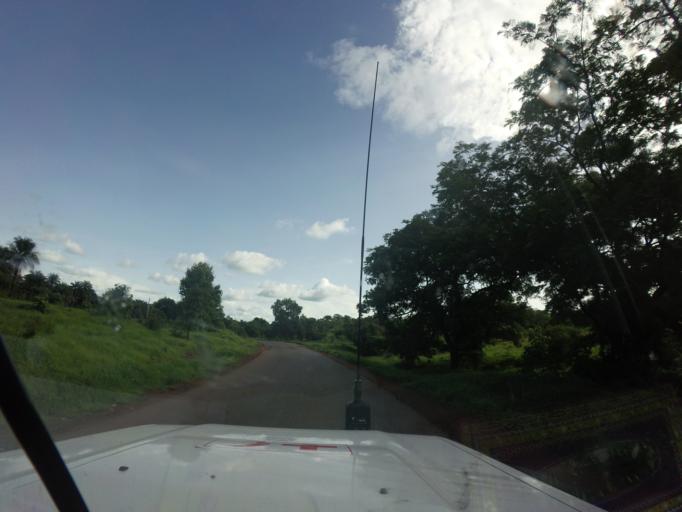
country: GN
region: Kindia
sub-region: Kindia
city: Kindia
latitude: 10.1221
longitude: -12.5461
